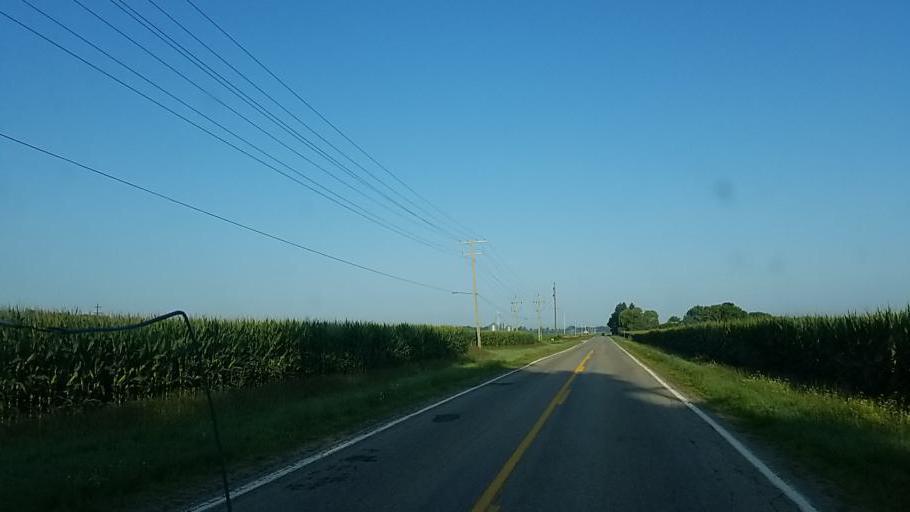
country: US
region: Michigan
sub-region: Montcalm County
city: Howard City
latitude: 43.3593
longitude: -85.3708
